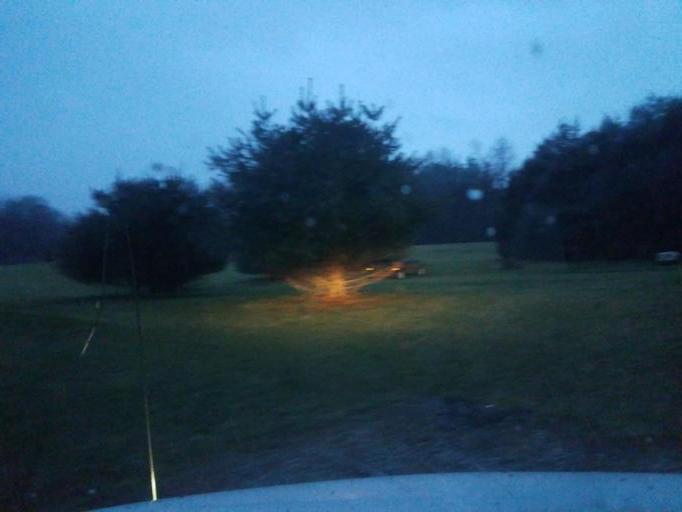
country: US
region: Ohio
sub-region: Knox County
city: Gambier
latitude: 40.3204
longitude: -82.4528
